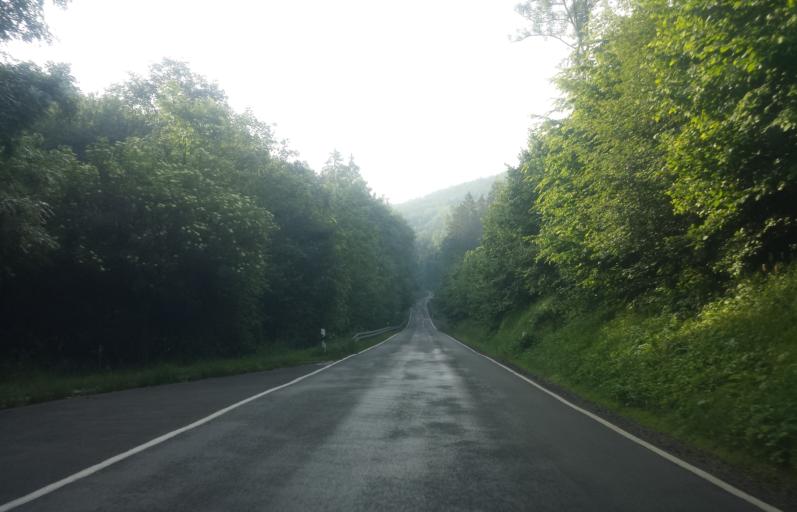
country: DE
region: Bavaria
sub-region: Upper Franconia
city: Ebermannstadt
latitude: 49.7858
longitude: 11.2082
